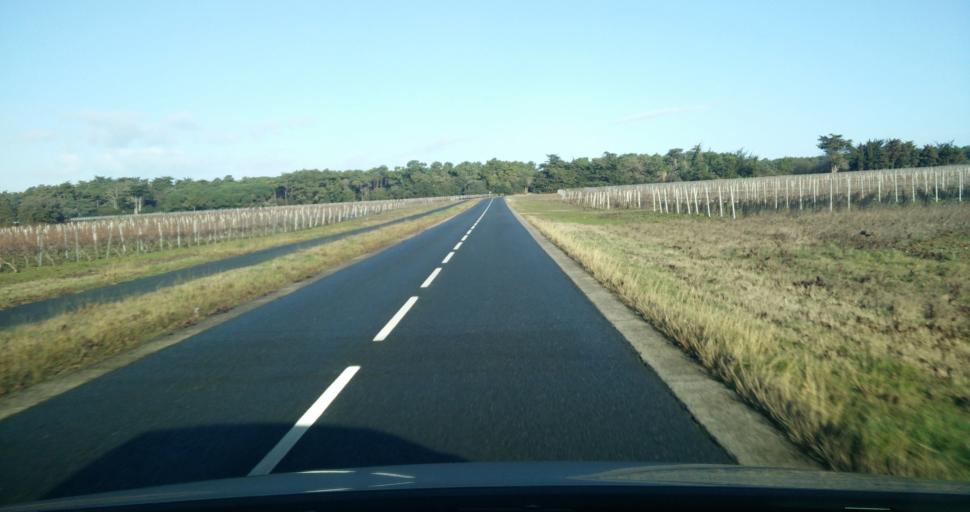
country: FR
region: Poitou-Charentes
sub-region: Departement de la Charente-Maritime
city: Sainte-Marie-de-Re
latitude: 46.1653
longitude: -1.3234
